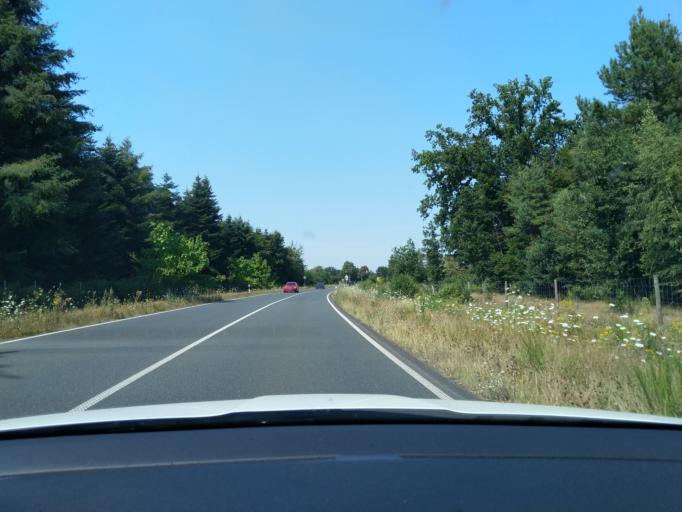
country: DE
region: North Rhine-Westphalia
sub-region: Regierungsbezirk Koln
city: Wassenberg
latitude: 51.1292
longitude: 6.1943
